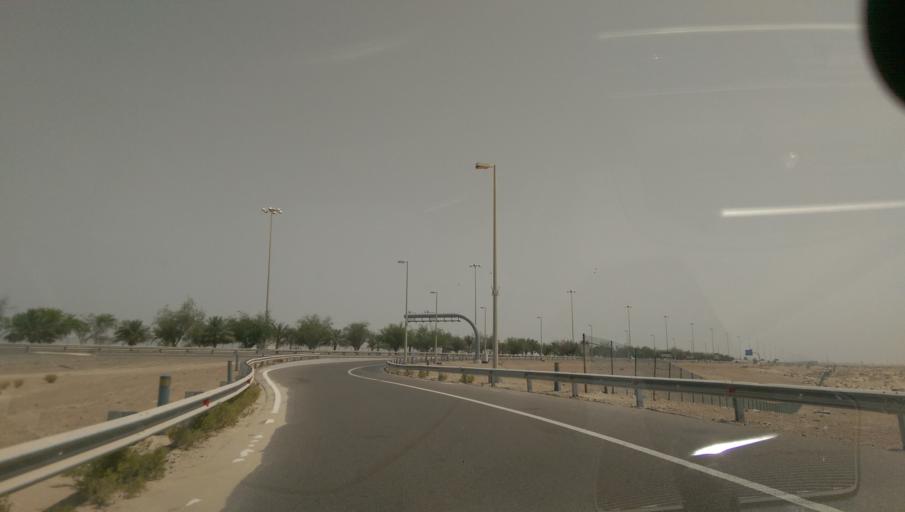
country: AE
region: Abu Dhabi
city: Abu Dhabi
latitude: 24.3893
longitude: 54.6647
